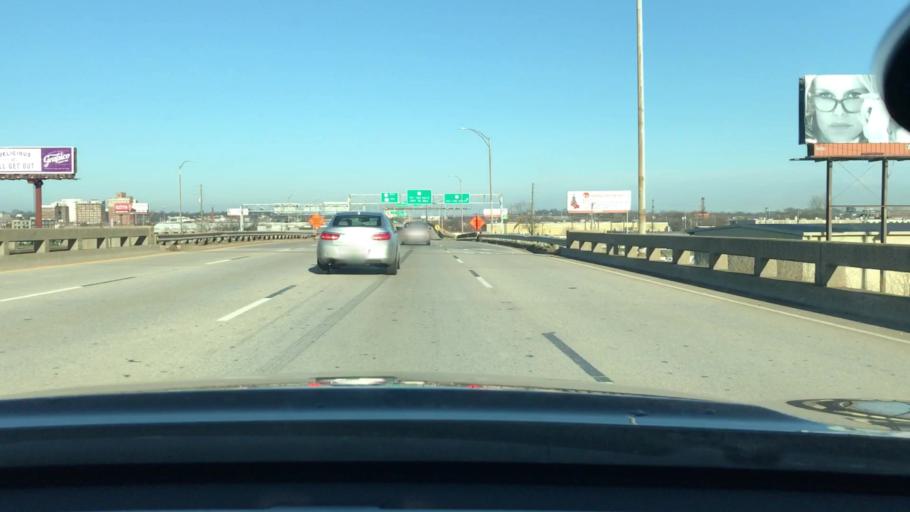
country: US
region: Alabama
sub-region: Jefferson County
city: Birmingham
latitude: 33.5123
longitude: -86.7931
